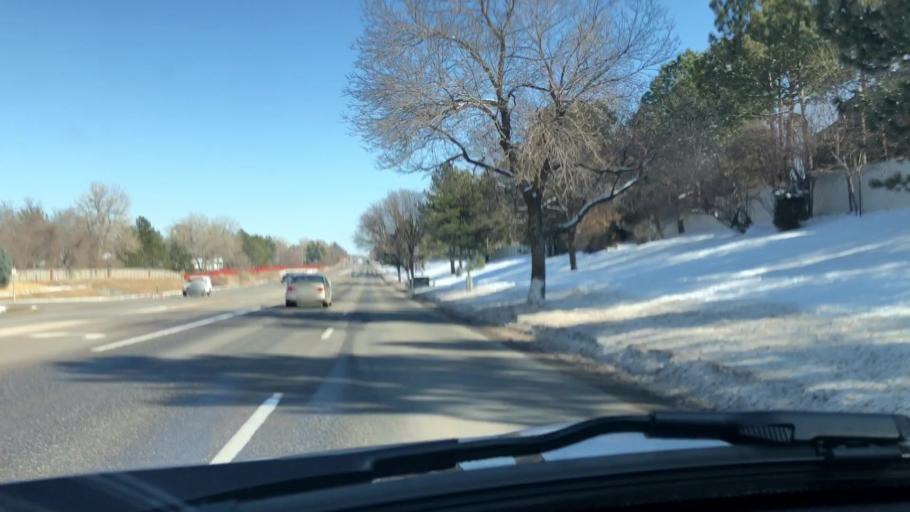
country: US
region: Colorado
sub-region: Arapahoe County
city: Castlewood
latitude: 39.5950
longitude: -104.9162
